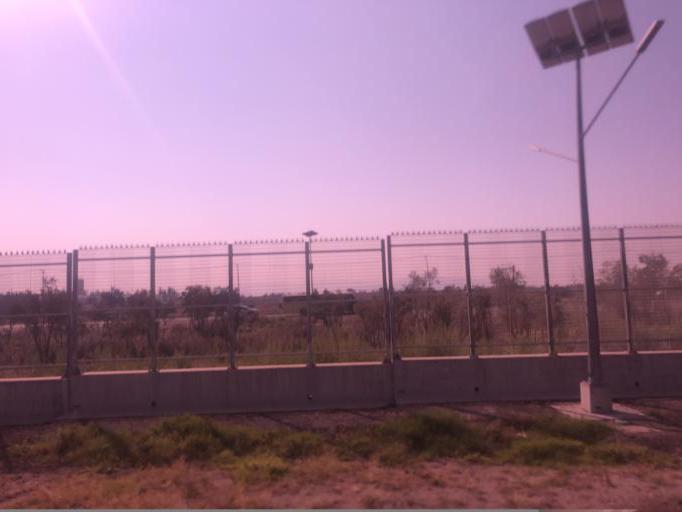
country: MX
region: Mexico
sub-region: Texcoco
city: Colonia Guadalupe Victoria
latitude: 19.4802
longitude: -98.9771
